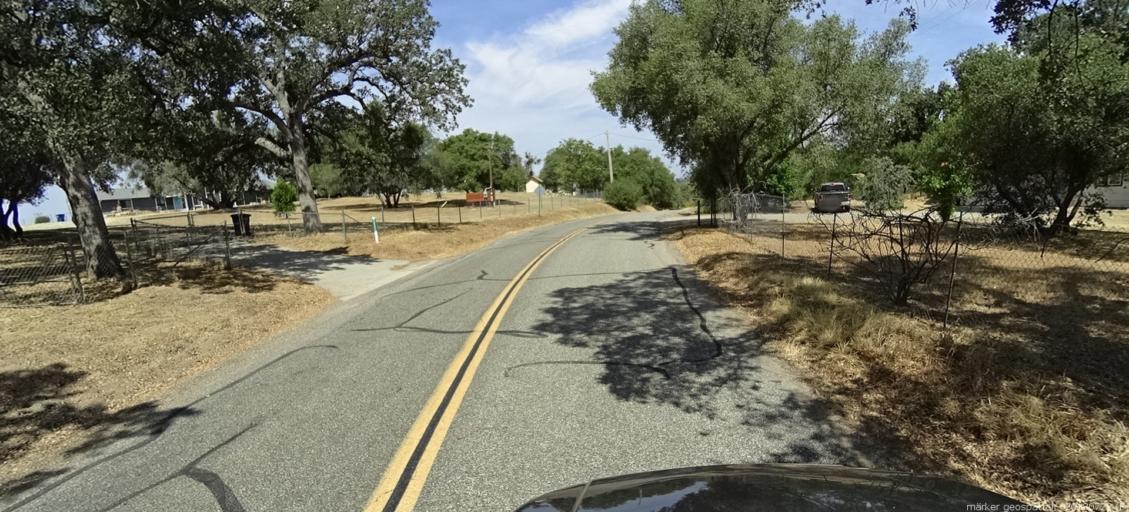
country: US
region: California
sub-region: Madera County
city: Coarsegold
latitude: 37.2563
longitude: -119.7359
